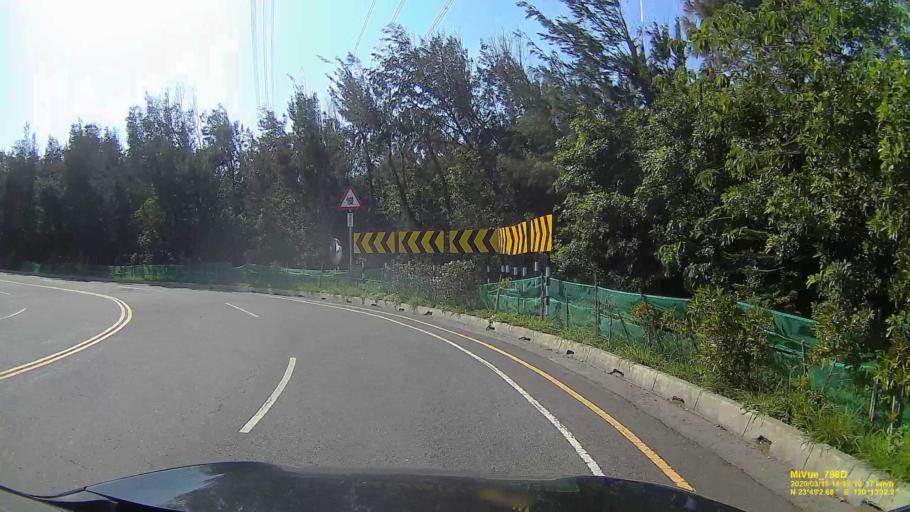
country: TW
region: Taiwan
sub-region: Yunlin
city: Douliu
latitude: 23.8174
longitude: 120.2255
